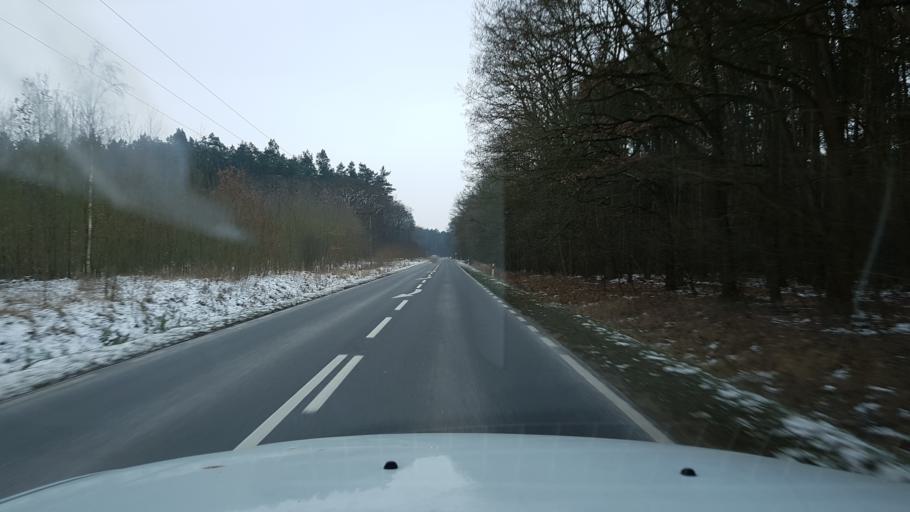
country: PL
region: West Pomeranian Voivodeship
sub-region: Powiat gryfinski
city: Chojna
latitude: 52.9317
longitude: 14.3771
